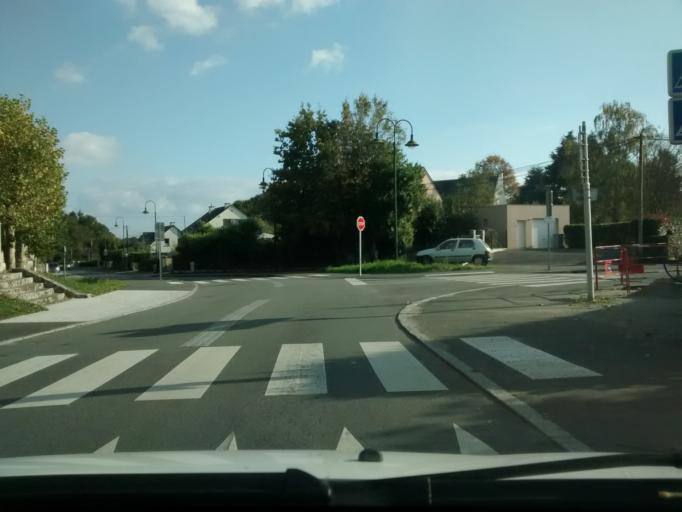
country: FR
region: Pays de la Loire
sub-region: Departement de la Loire-Atlantique
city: Orvault
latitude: 47.2752
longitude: -1.6371
